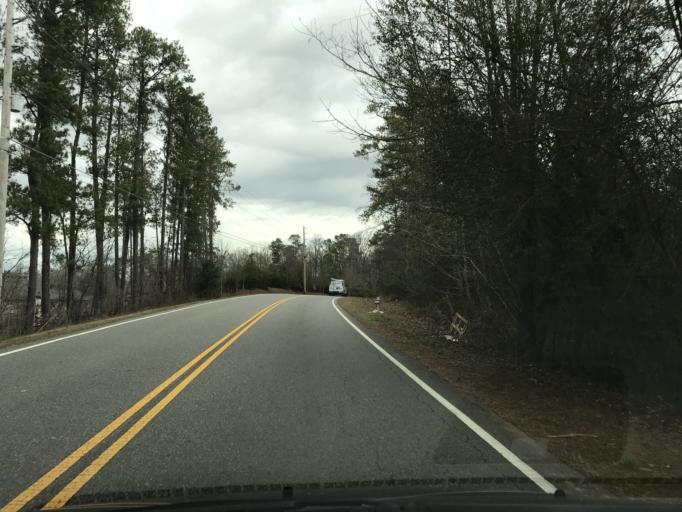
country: US
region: Georgia
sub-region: Fulton County
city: Milton
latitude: 34.1220
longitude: -84.3285
